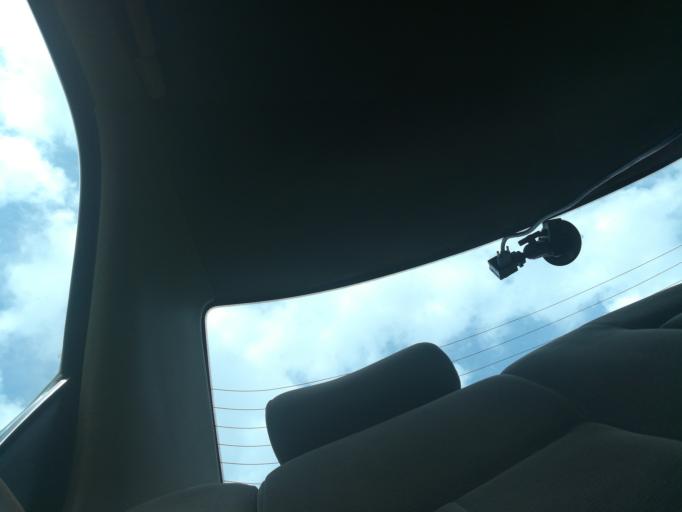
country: NG
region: Lagos
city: Ikorodu
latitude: 6.6635
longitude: 3.6120
